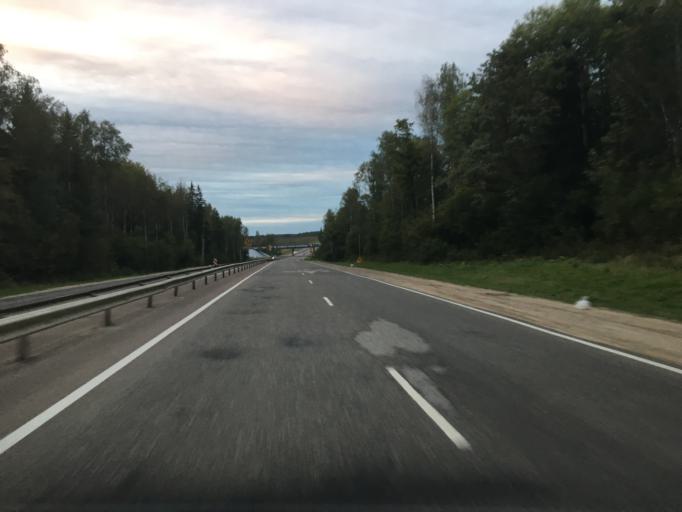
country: RU
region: Kaluga
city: Kaluga
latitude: 54.6431
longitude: 36.2975
